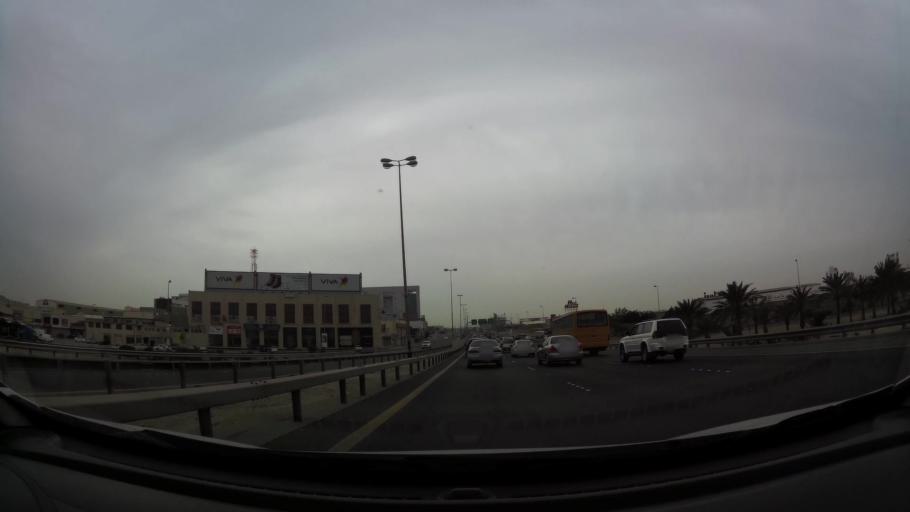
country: BH
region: Northern
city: Madinat `Isa
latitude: 26.1933
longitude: 50.5351
